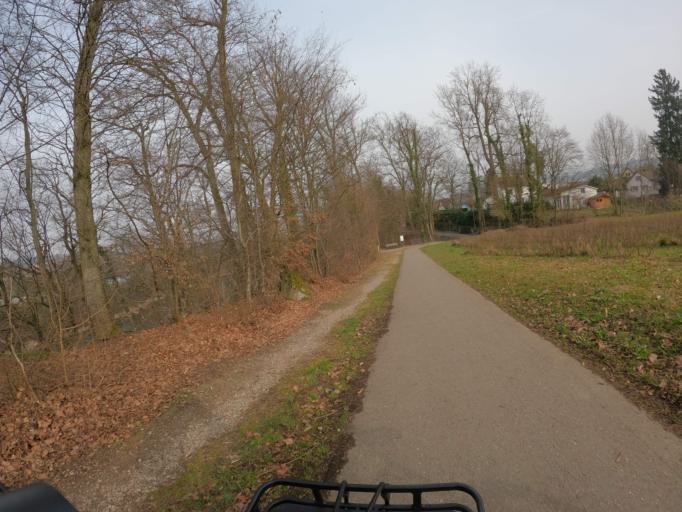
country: CH
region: Aargau
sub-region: Bezirk Bremgarten
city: Bremgarten
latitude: 47.3451
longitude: 8.3467
